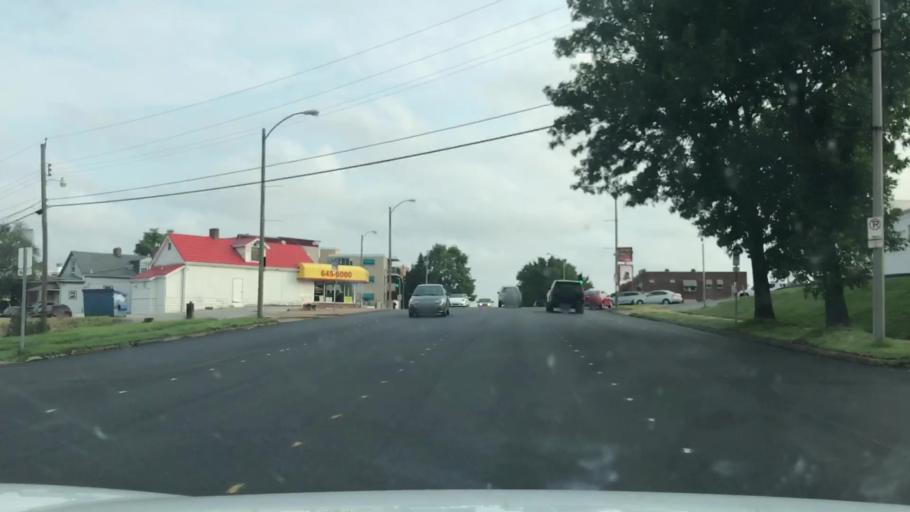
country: US
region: Missouri
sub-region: Saint Louis County
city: Maplewood
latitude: 38.6081
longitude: -90.2885
